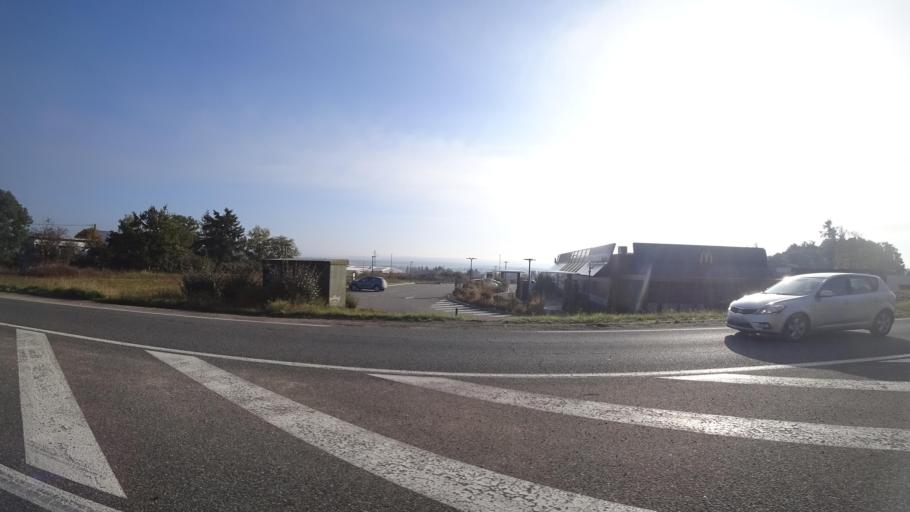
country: FR
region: Midi-Pyrenees
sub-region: Departement de l'Aveyron
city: Luc-la-Primaube
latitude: 44.3143
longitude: 2.5578
